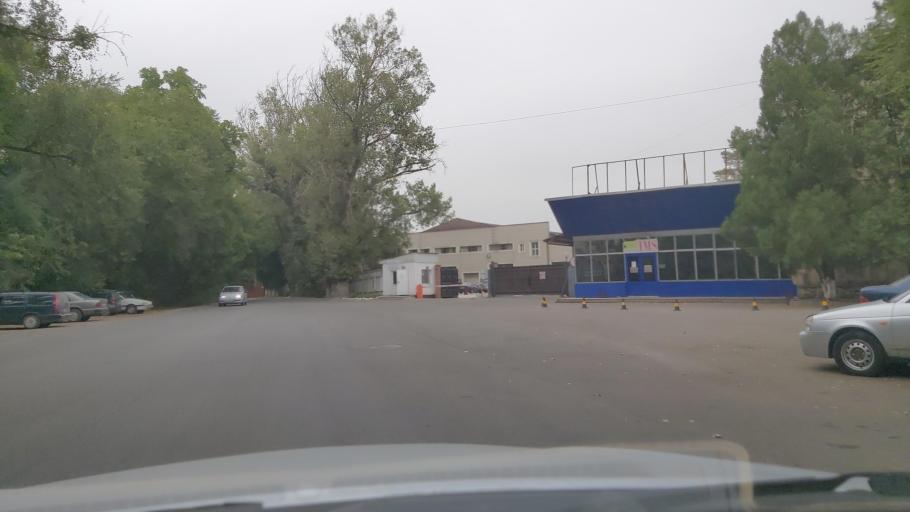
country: KZ
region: Almaty Oblysy
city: Pervomayskiy
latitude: 43.3527
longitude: 76.9782
